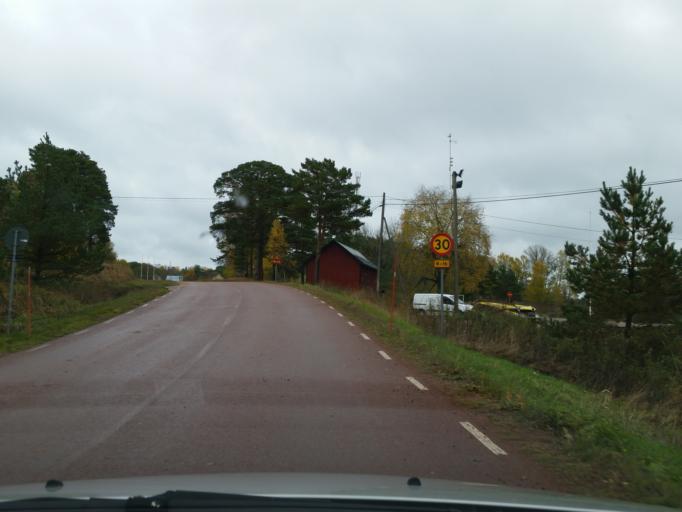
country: AX
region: Alands landsbygd
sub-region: Lumparland
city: Lumparland
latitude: 60.1175
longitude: 20.2549
